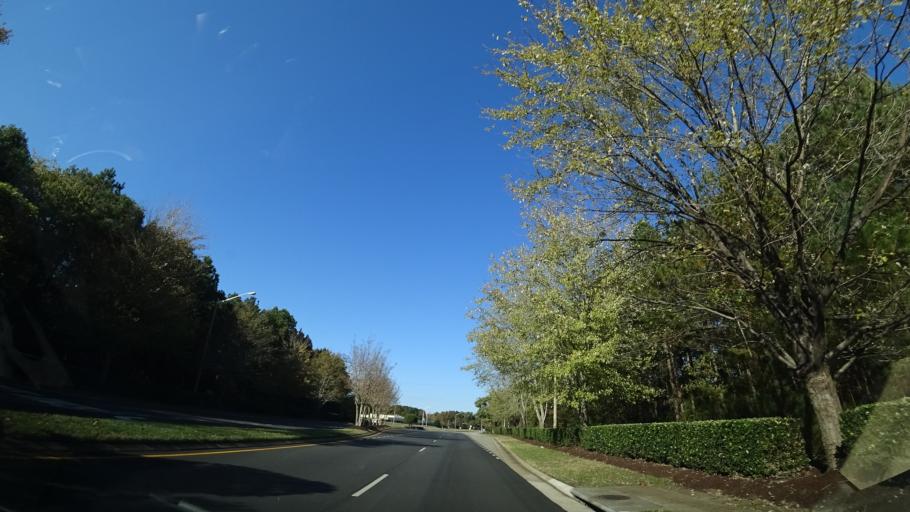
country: US
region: Virginia
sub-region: City of Newport News
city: Newport News
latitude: 36.8891
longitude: -76.4373
